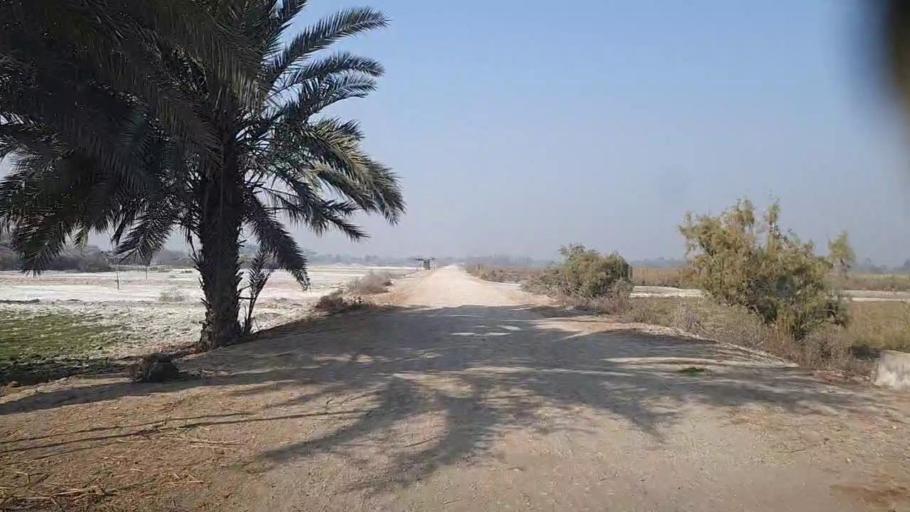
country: PK
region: Sindh
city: Karaundi
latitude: 26.8474
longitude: 68.3952
